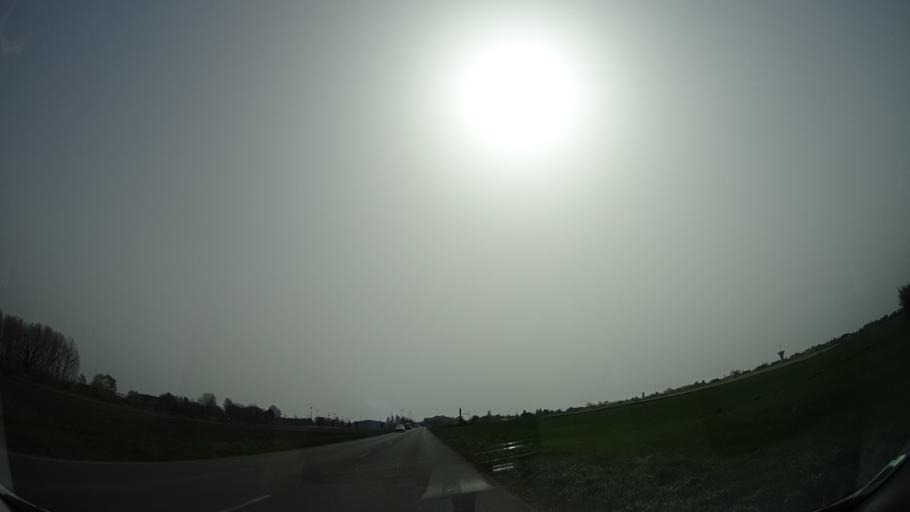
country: FR
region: Pays de la Loire
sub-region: Departement de Maine-et-Loire
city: Doue-la-Fontaine
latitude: 47.2043
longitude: -0.2888
